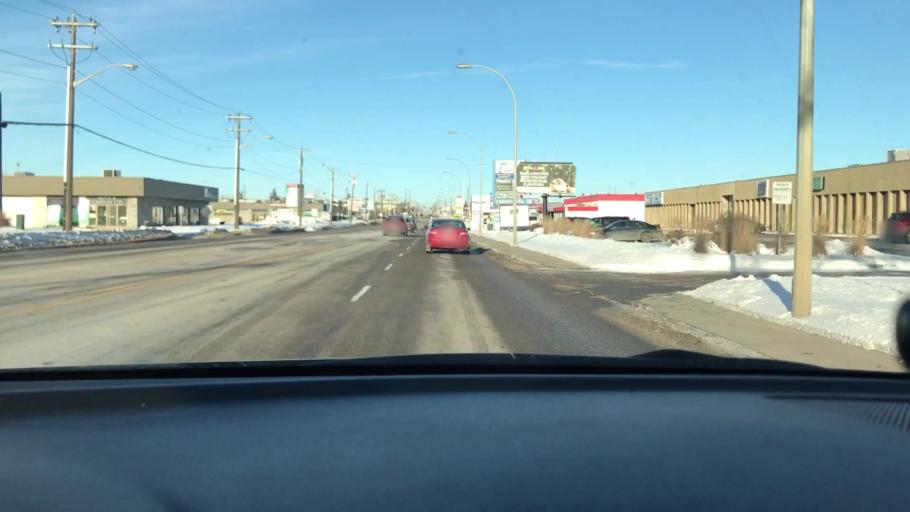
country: CA
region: Alberta
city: Edmonton
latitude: 53.4835
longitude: -113.4860
